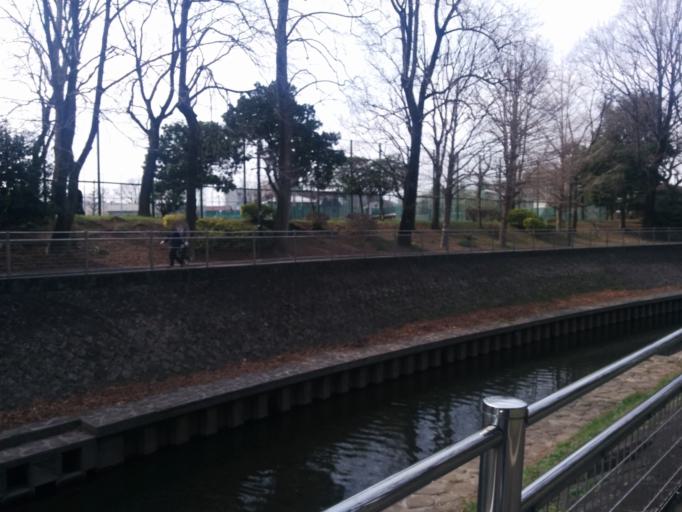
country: JP
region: Tokyo
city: Tokyo
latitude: 35.6899
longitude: 139.6327
